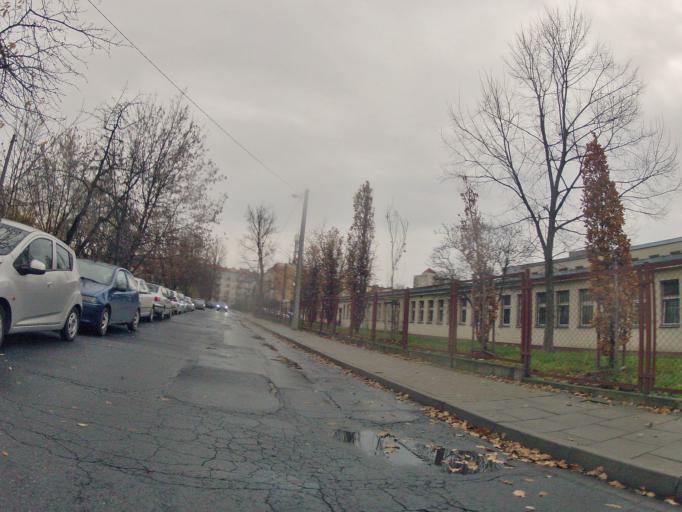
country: PL
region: Lesser Poland Voivodeship
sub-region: Krakow
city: Krakow
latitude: 50.0704
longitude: 20.0177
